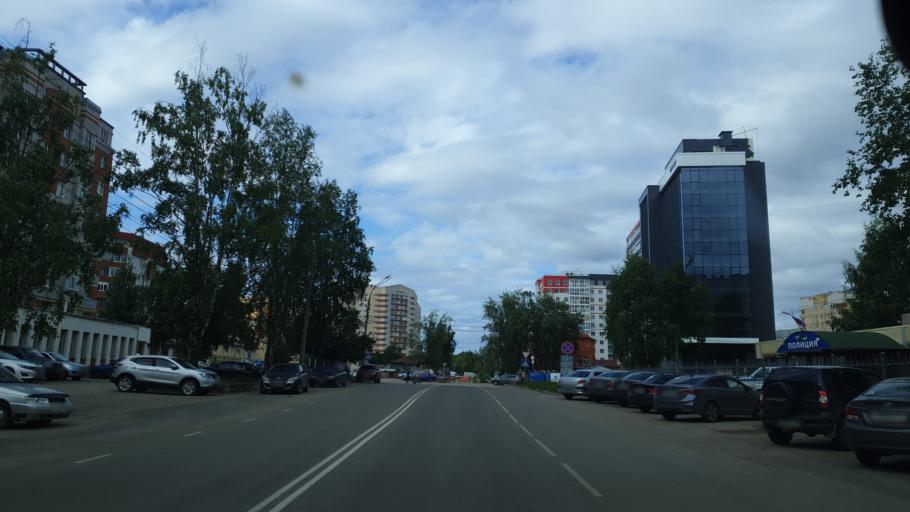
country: RU
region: Komi Republic
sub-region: Syktyvdinskiy Rayon
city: Syktyvkar
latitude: 61.6740
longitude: 50.8246
